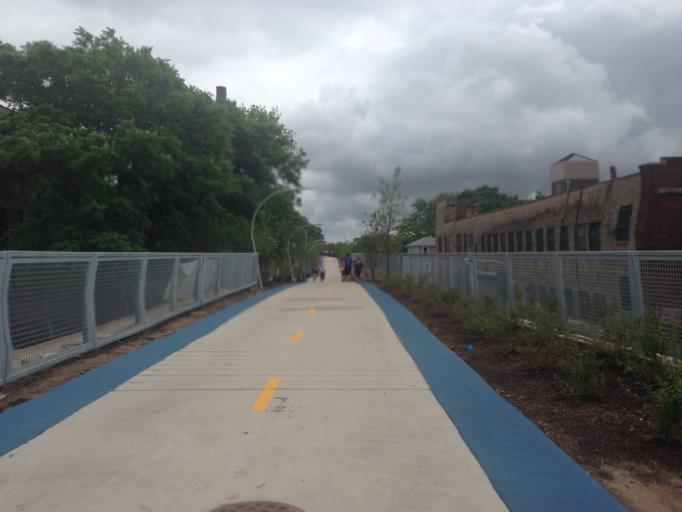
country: US
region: Illinois
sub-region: Cook County
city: Oak Park
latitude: 41.9136
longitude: -87.7168
